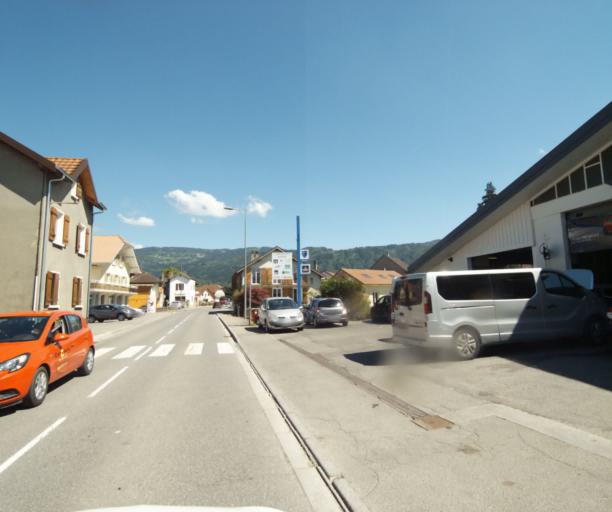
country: FR
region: Rhone-Alpes
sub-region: Departement de la Haute-Savoie
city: Bons-en-Chablais
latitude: 46.2698
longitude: 6.3650
